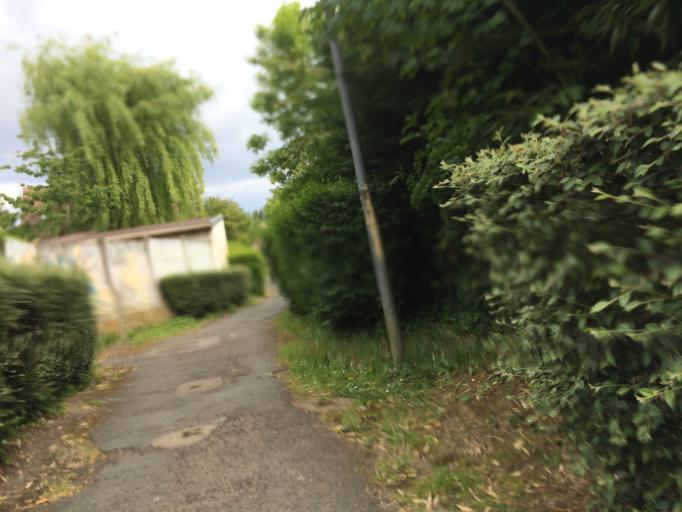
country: FR
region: Ile-de-France
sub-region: Departement de l'Essonne
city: Saint-Michel-sur-Orge
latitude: 48.6328
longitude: 2.3103
